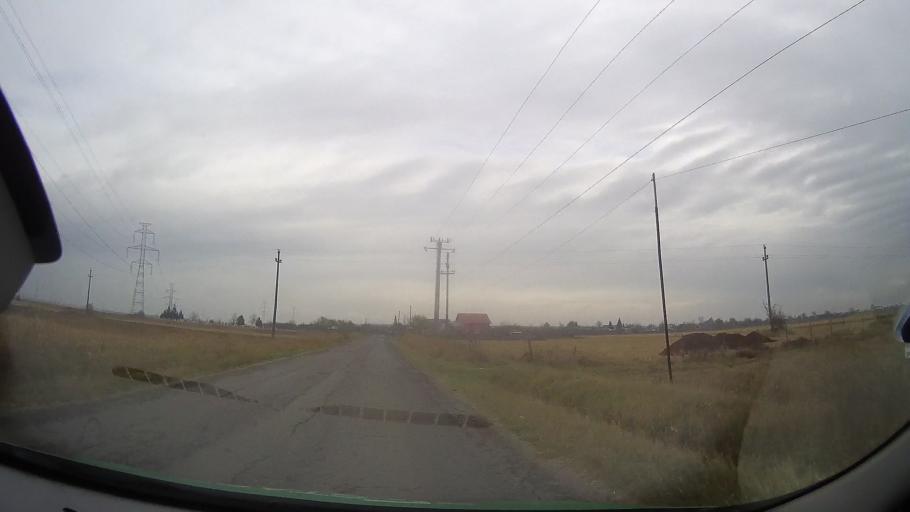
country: RO
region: Prahova
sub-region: Comuna Valea Calugareasca
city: Pantazi
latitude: 44.9259
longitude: 26.1533
